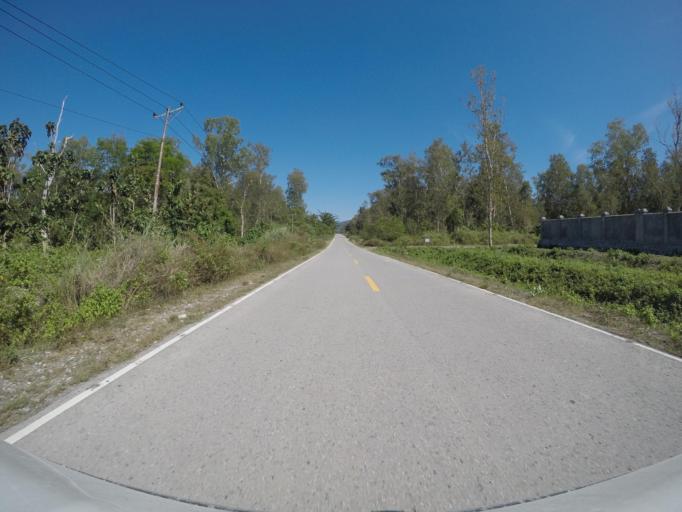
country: TL
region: Viqueque
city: Viqueque
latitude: -8.9669
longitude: 126.0240
